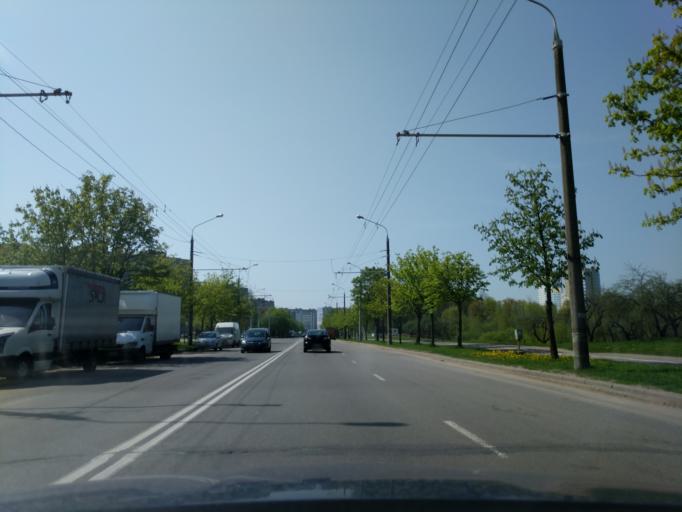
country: BY
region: Minsk
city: Novoye Medvezhino
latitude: 53.8685
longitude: 27.4584
